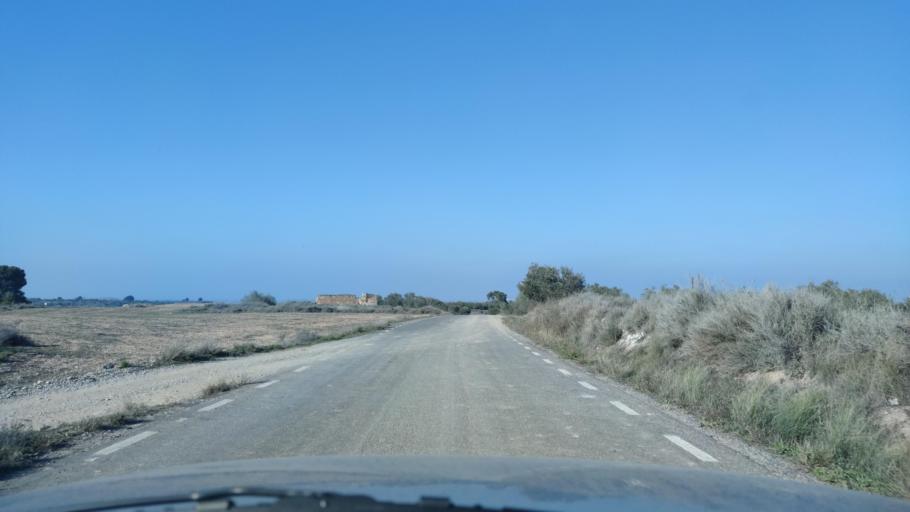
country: ES
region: Catalonia
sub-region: Provincia de Lleida
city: Torrebesses
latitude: 41.4497
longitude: 0.5583
